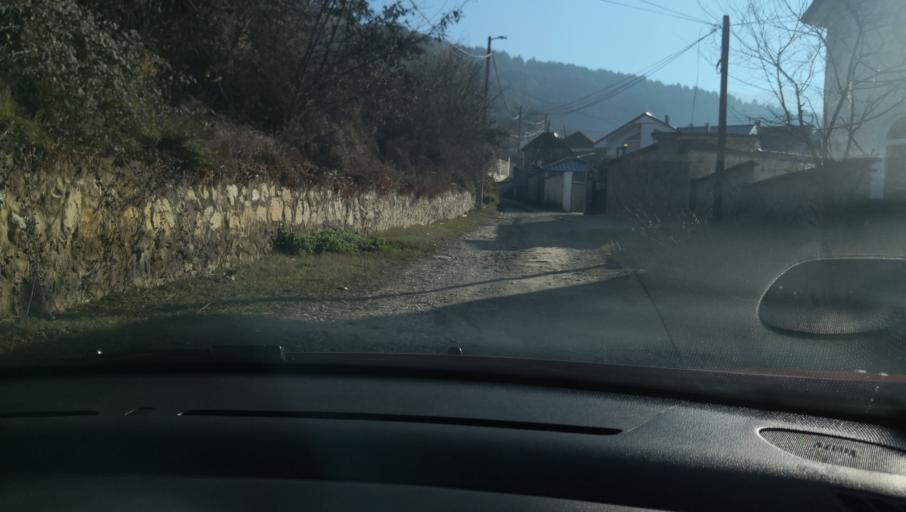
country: MK
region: Brvenica
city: Celopek
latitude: 41.9252
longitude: 21.0205
